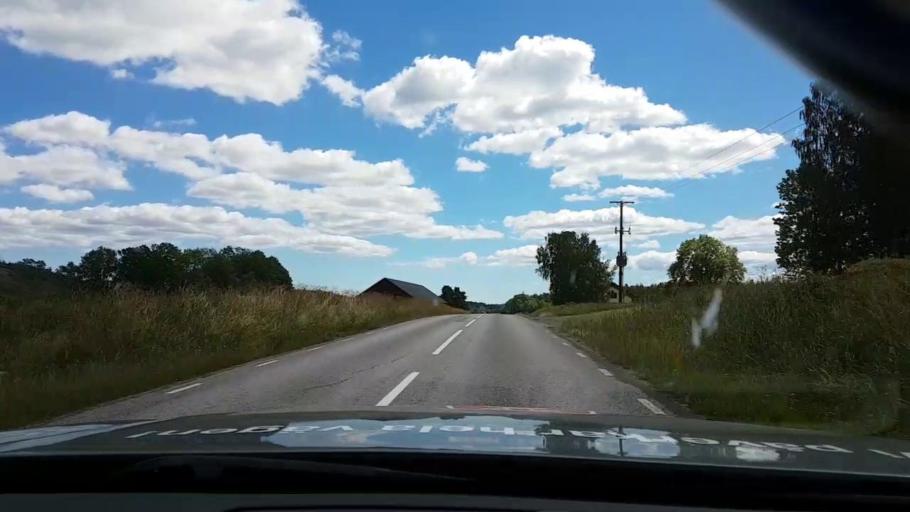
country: SE
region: Kalmar
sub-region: Vasterviks Kommun
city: Forserum
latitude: 58.0482
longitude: 16.4104
